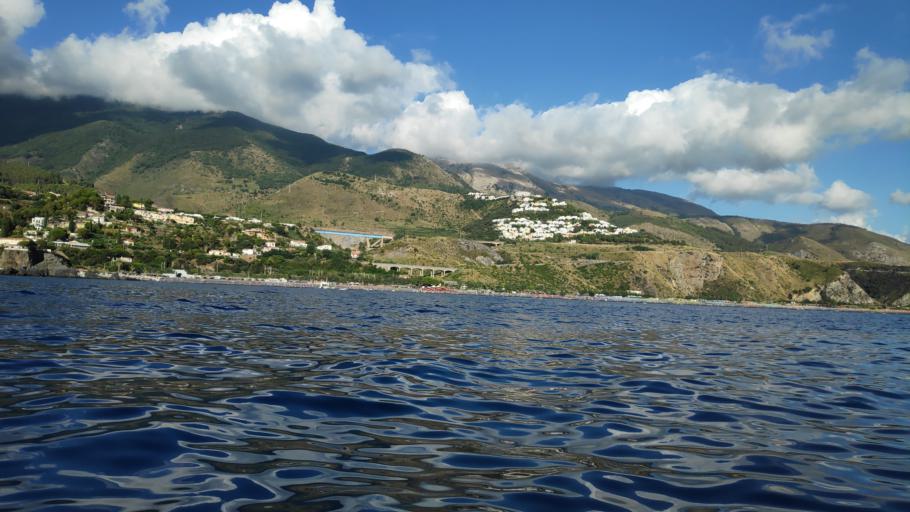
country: IT
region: Calabria
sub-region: Provincia di Cosenza
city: Praia a Mare
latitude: 39.8700
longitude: 15.7815
